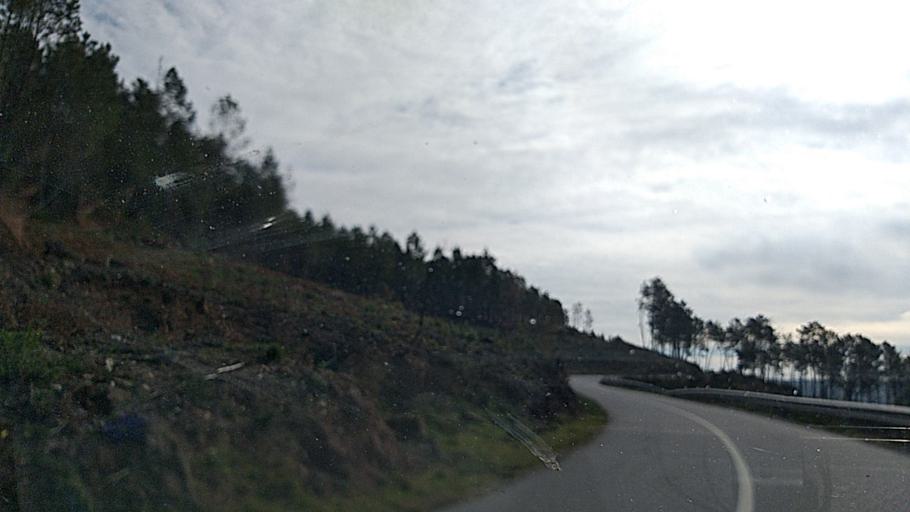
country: PT
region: Guarda
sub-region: Fornos de Algodres
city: Fornos de Algodres
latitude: 40.6863
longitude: -7.5399
